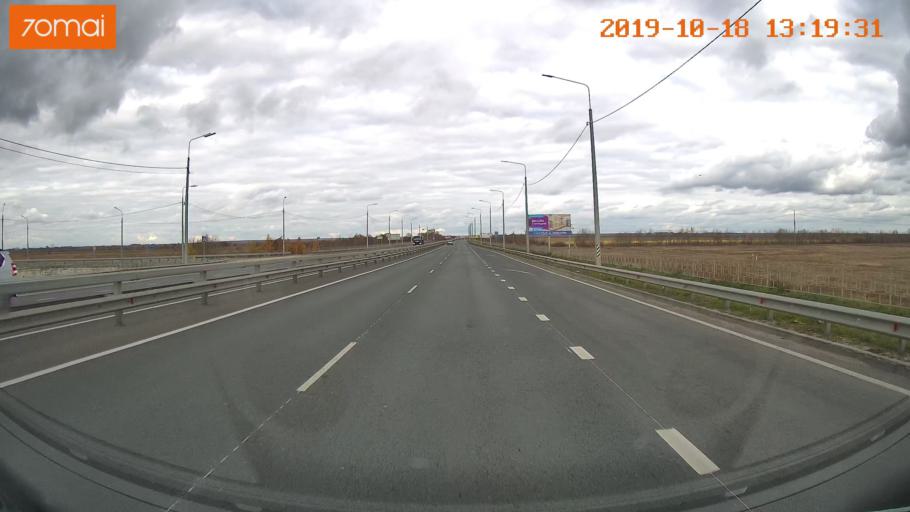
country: RU
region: Rjazan
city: Polyany
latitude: 54.6683
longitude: 39.8254
